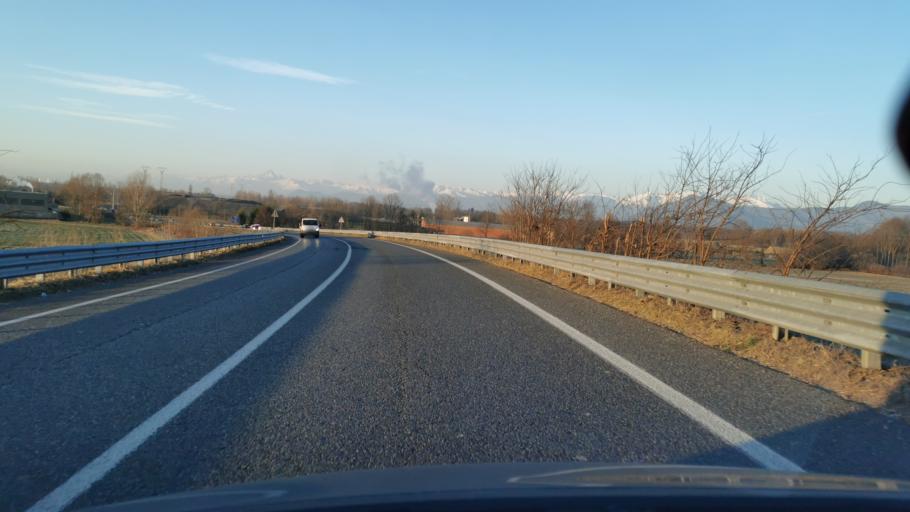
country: IT
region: Piedmont
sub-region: Provincia di Torino
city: Borgaro Torinese
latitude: 45.1577
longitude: 7.6466
